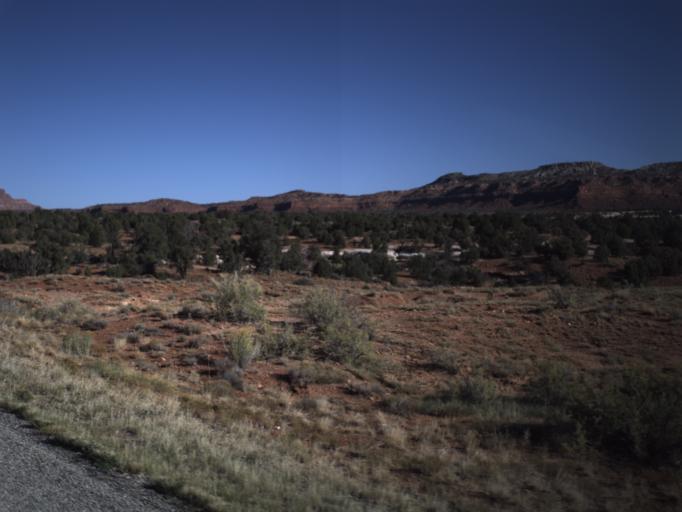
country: US
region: Utah
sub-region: San Juan County
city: Blanding
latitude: 37.6421
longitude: -110.1636
